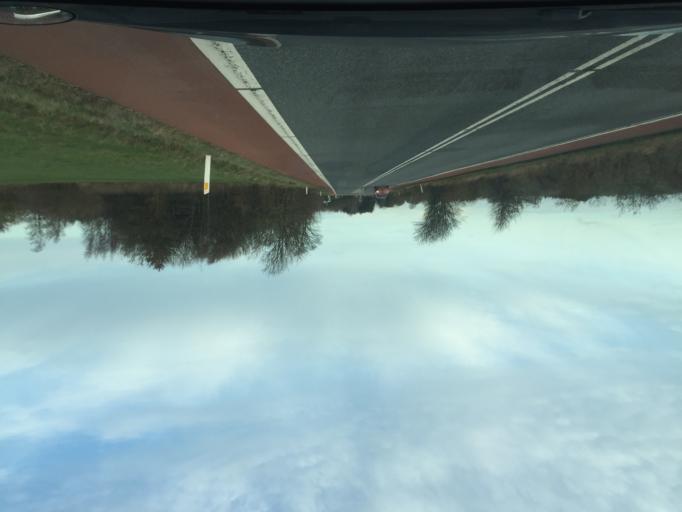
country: DK
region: South Denmark
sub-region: Faaborg-Midtfyn Kommune
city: Ringe
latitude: 55.2605
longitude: 10.4639
